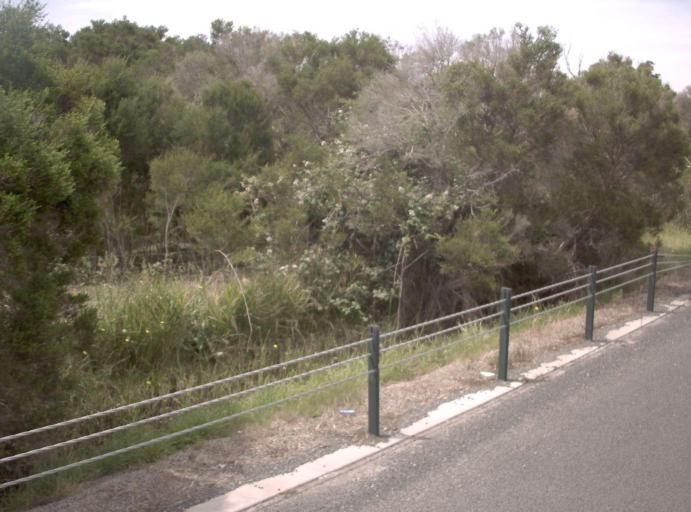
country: AU
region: Victoria
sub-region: Mornington Peninsula
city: Tyabb
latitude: -38.2265
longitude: 145.2172
